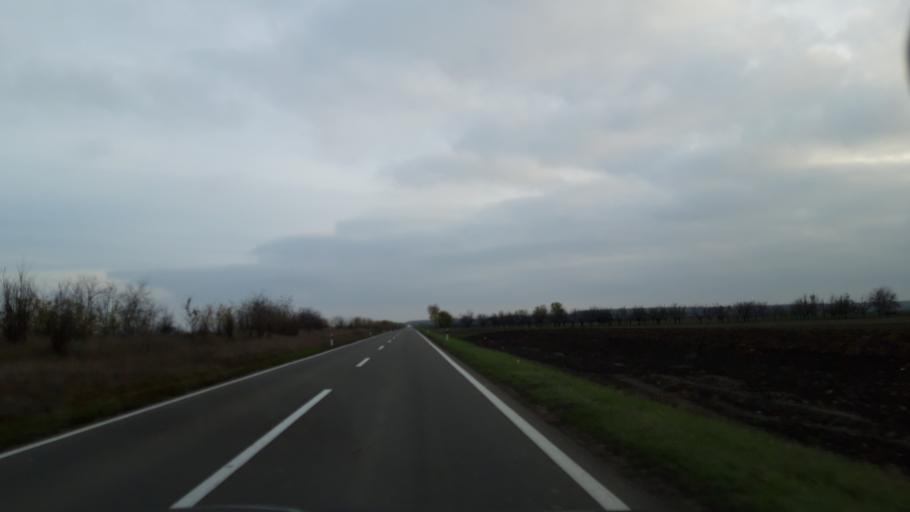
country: RS
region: Autonomna Pokrajina Vojvodina
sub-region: Severnobanatski Okrug
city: Novi Knezevac
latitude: 46.0141
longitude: 20.0979
